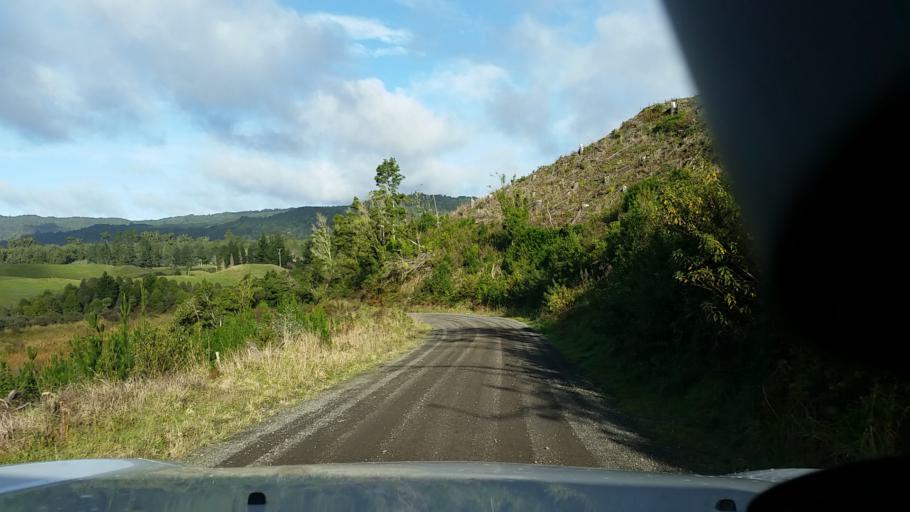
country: NZ
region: Bay of Plenty
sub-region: Kawerau District
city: Kawerau
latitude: -38.0350
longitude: 176.5518
